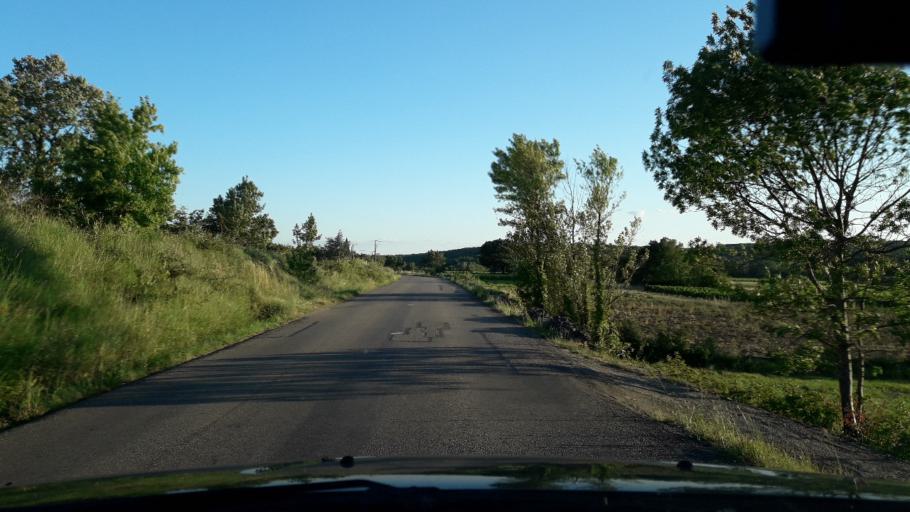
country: FR
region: Rhone-Alpes
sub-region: Departement de l'Ardeche
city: Lavilledieu
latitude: 44.6006
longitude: 4.4647
